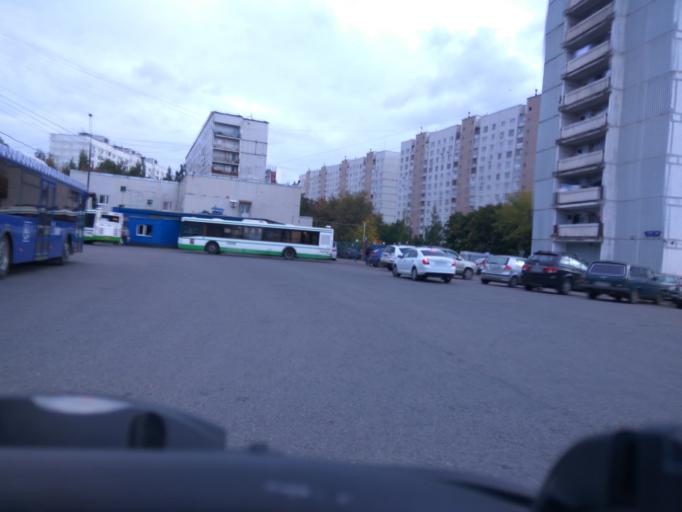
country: RU
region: Moscow
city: Kozeyevo
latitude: 55.8764
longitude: 37.6192
